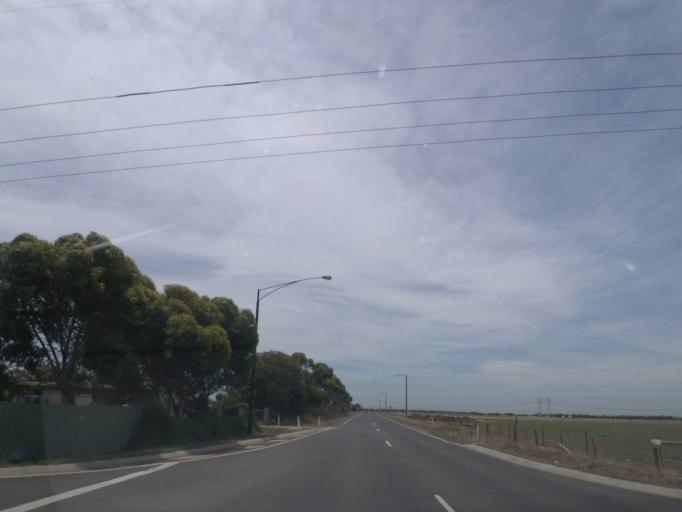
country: AU
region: Victoria
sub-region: Melton
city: Caroline Springs
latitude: -37.7415
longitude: 144.7063
